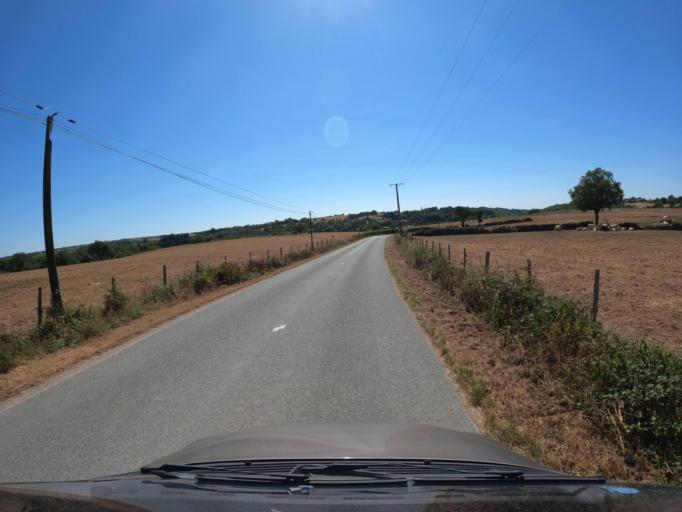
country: FR
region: Pays de la Loire
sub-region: Departement de la Vendee
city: Saint-Aubin-des-Ormeaux
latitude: 47.0053
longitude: -1.0076
